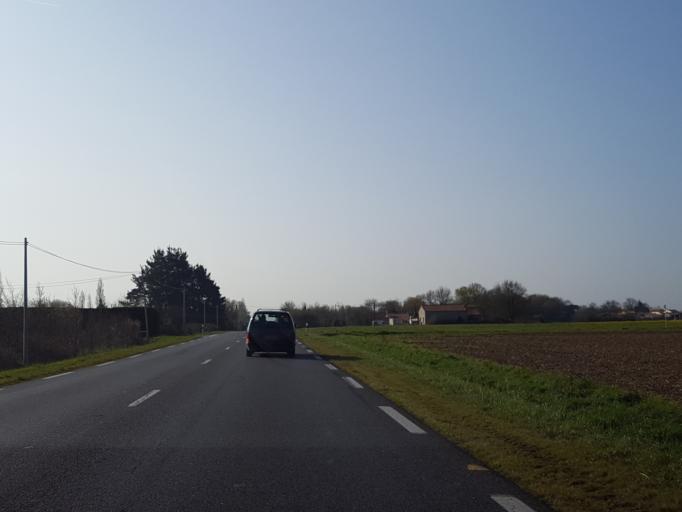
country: FR
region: Pays de la Loire
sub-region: Departement de la Loire-Atlantique
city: Le Bignon
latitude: 47.1005
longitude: -1.5342
